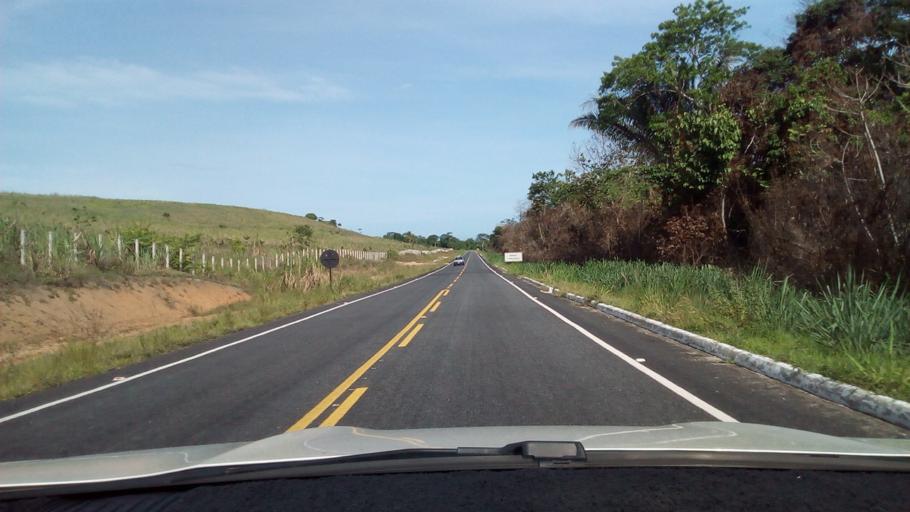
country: BR
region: Paraiba
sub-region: Bayeux
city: Bayeux
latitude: -7.0628
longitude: -34.9249
